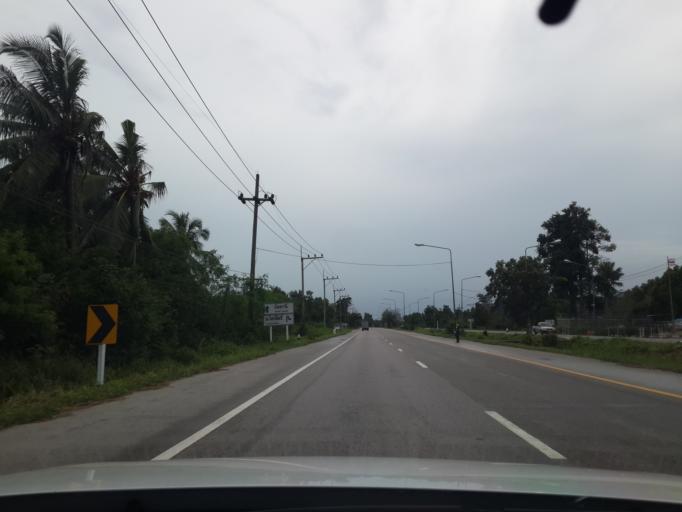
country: TH
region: Pattani
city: Khok Pho
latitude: 6.8127
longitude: 101.0977
